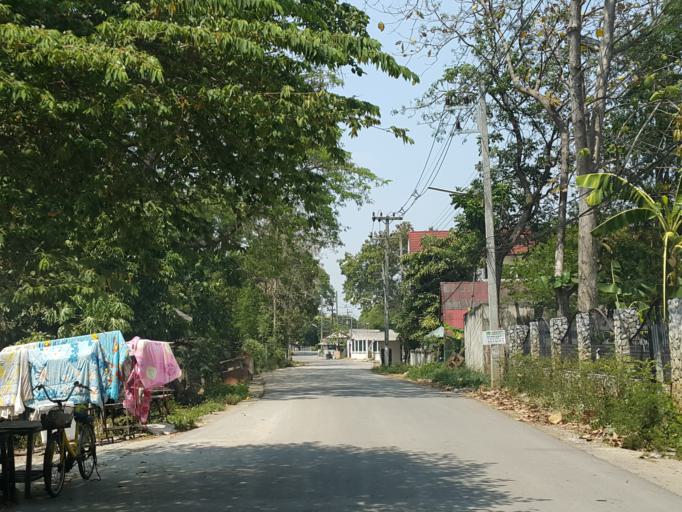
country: TH
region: Chiang Mai
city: Saraphi
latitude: 18.7365
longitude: 98.9912
